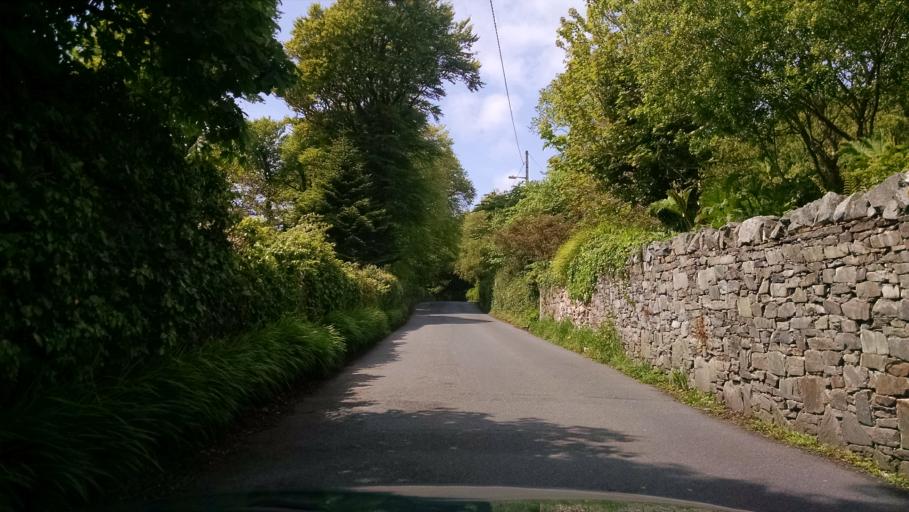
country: IE
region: Connaught
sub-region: County Galway
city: Clifden
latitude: 53.4890
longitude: -10.0276
